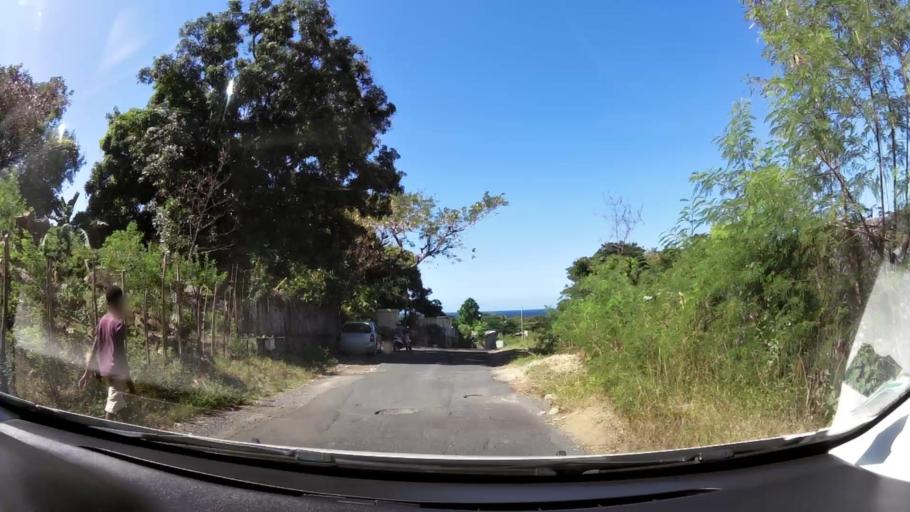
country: YT
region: Pamandzi
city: Pamandzi
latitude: -12.7995
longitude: 45.2842
